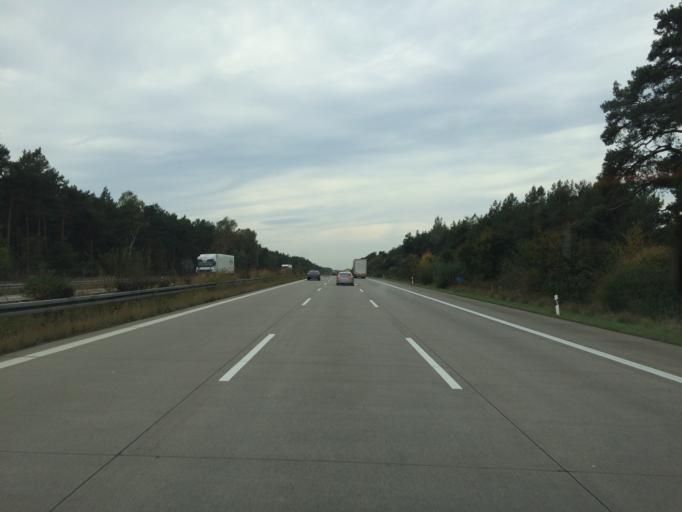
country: DE
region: Brandenburg
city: Graben
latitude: 52.2708
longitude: 12.3833
